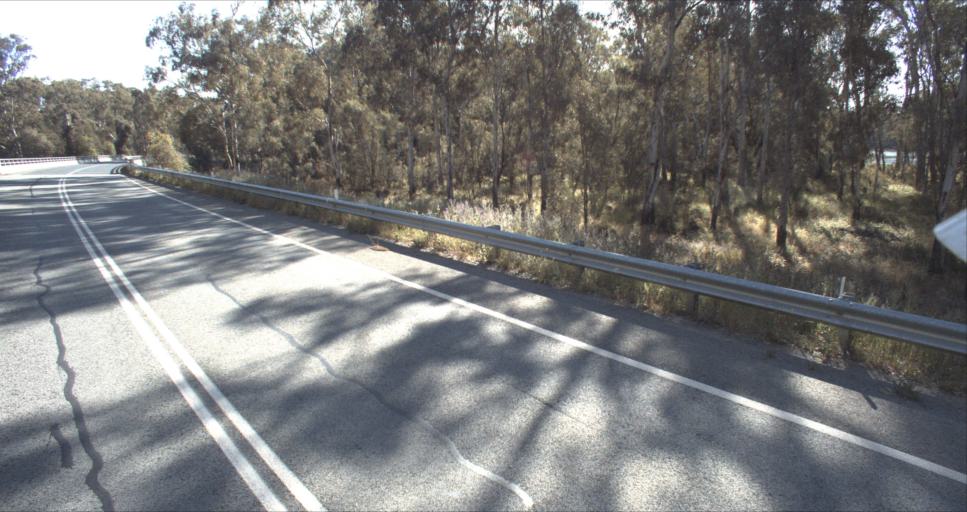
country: AU
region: New South Wales
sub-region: Leeton
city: Leeton
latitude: -34.6381
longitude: 146.3747
